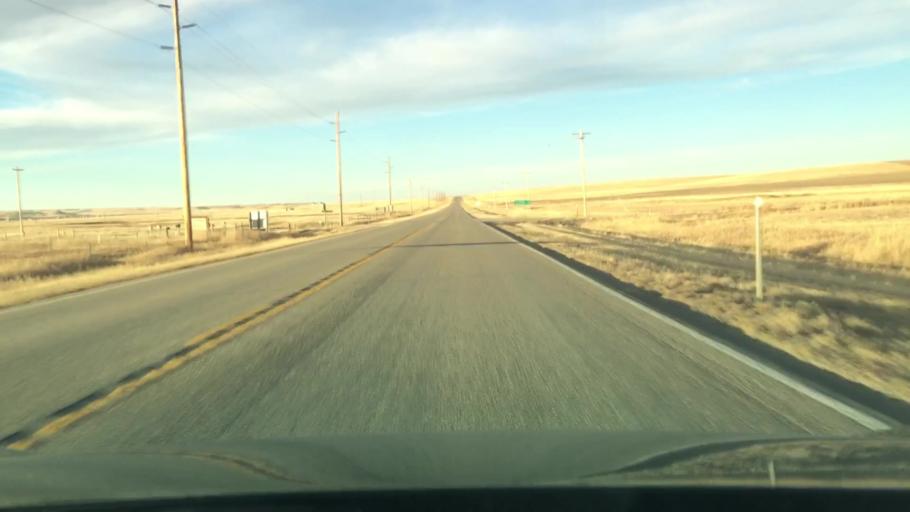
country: US
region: Montana
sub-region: Wheatland County
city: Harlowton
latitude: 46.8232
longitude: -109.7612
